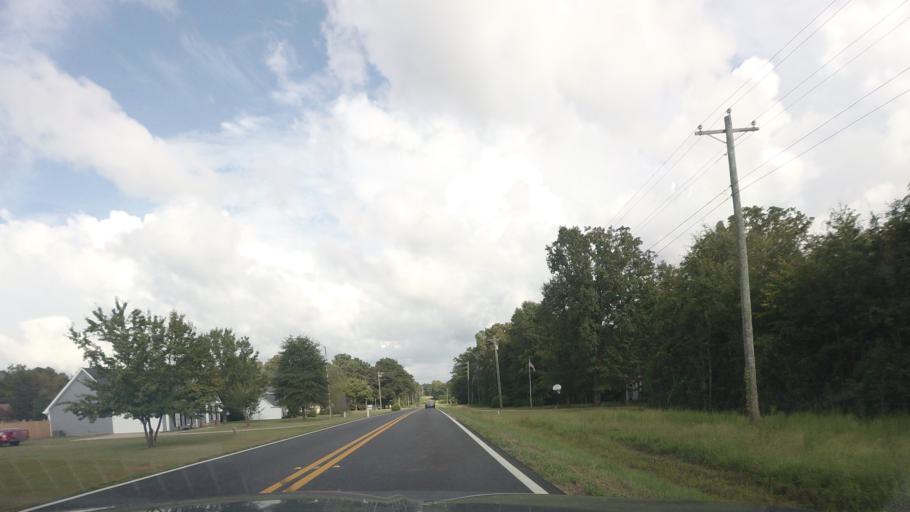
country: US
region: Georgia
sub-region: Houston County
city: Centerville
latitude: 32.6350
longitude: -83.7179
